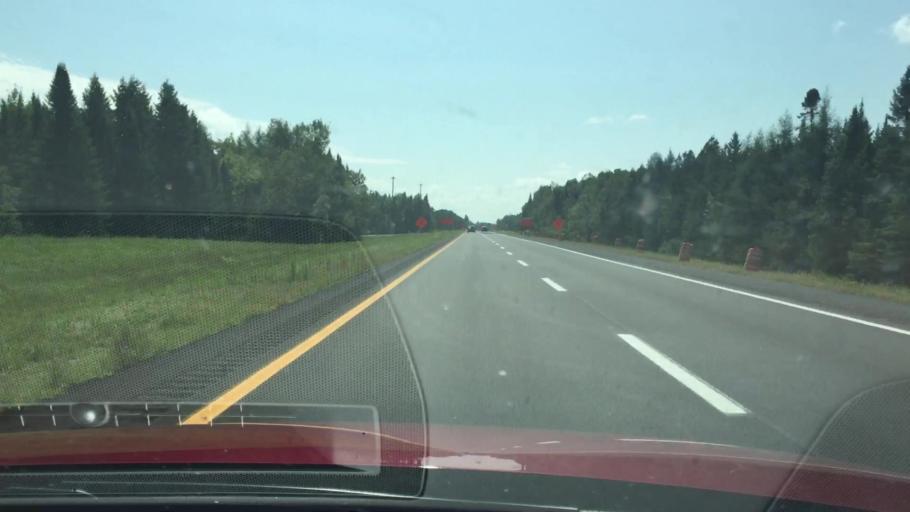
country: US
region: Maine
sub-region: Penobscot County
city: Patten
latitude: 45.8806
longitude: -68.4098
